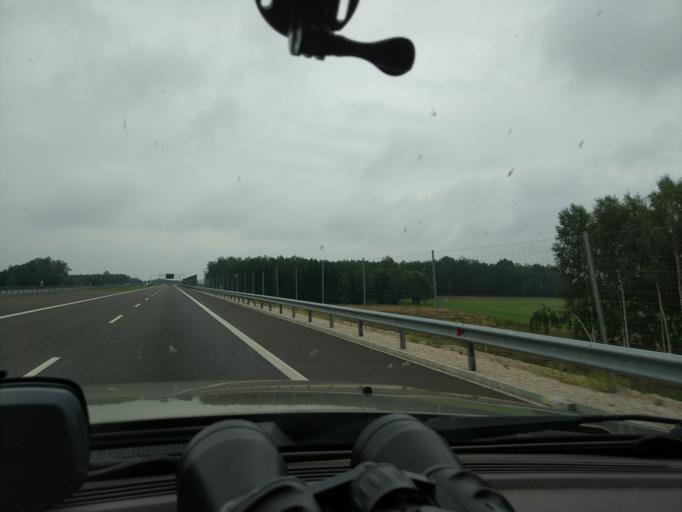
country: PL
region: Podlasie
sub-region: Powiat zambrowski
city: Szumowo
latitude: 52.9357
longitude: 22.1421
